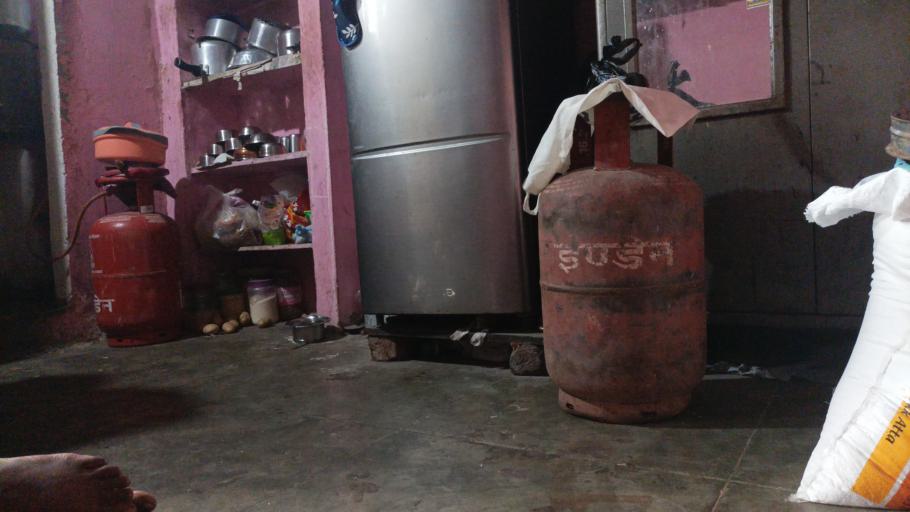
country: IN
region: Telangana
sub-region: Hyderabad
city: Hyderabad
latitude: 17.3880
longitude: 78.4926
